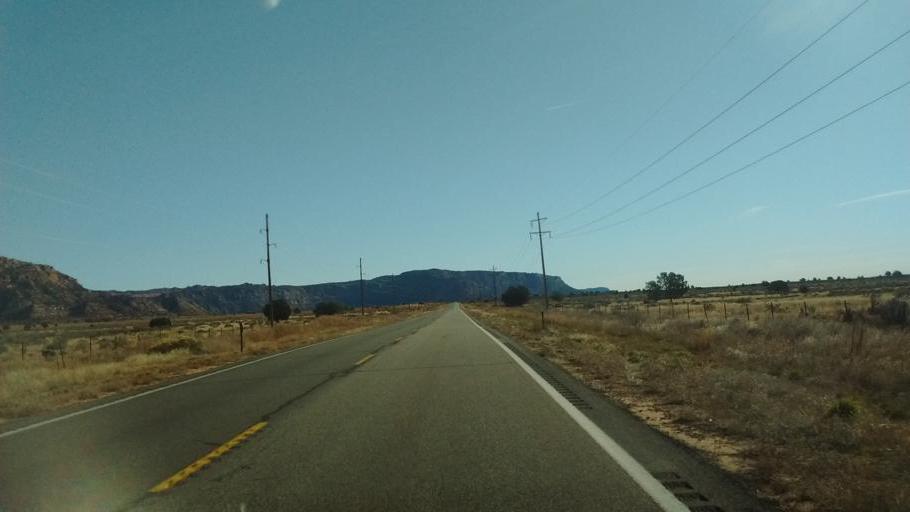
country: US
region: Arizona
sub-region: Mohave County
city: Colorado City
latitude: 37.0143
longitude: -113.0234
